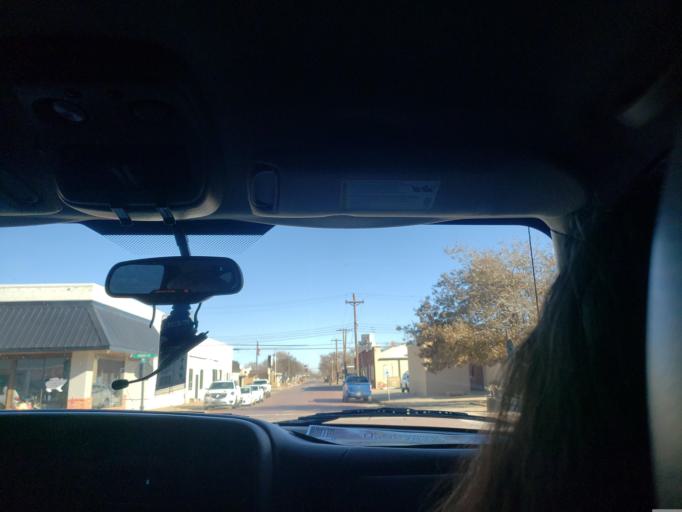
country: US
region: Texas
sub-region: Dallam County
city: Dalhart
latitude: 36.0622
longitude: -102.5233
